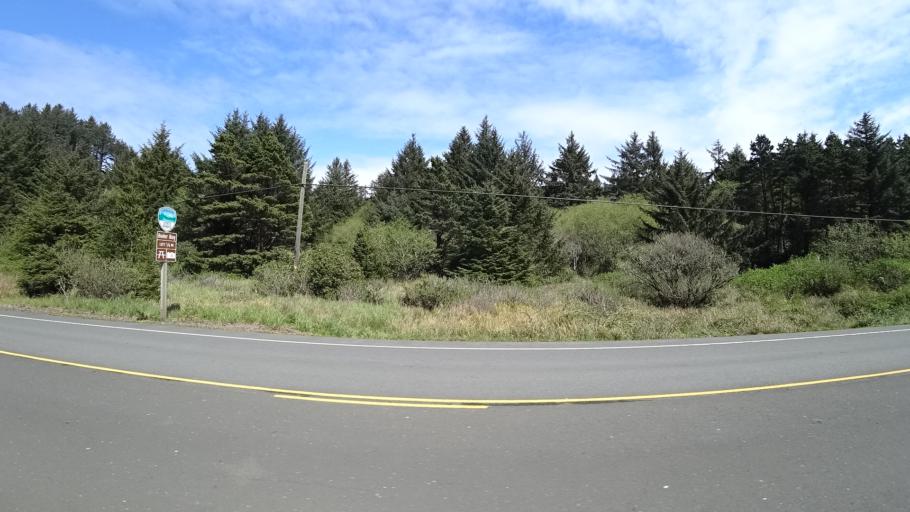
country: US
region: Oregon
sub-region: Lincoln County
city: Depoe Bay
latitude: 44.8242
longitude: -124.0652
